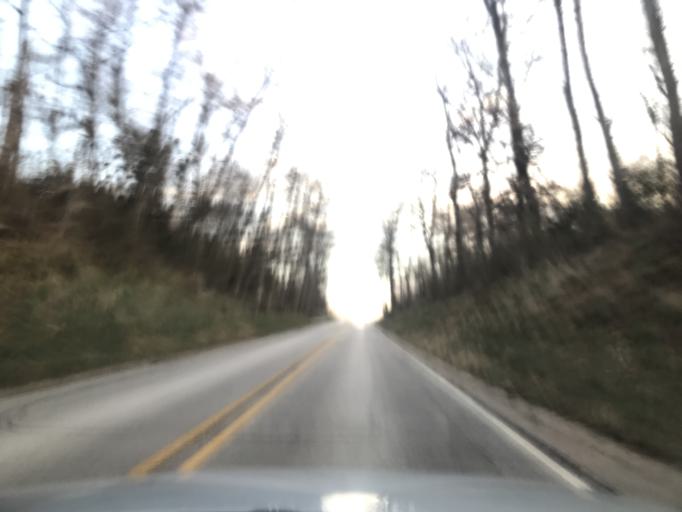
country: US
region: Illinois
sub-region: Henderson County
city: Oquawka
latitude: 40.9159
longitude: -90.8643
